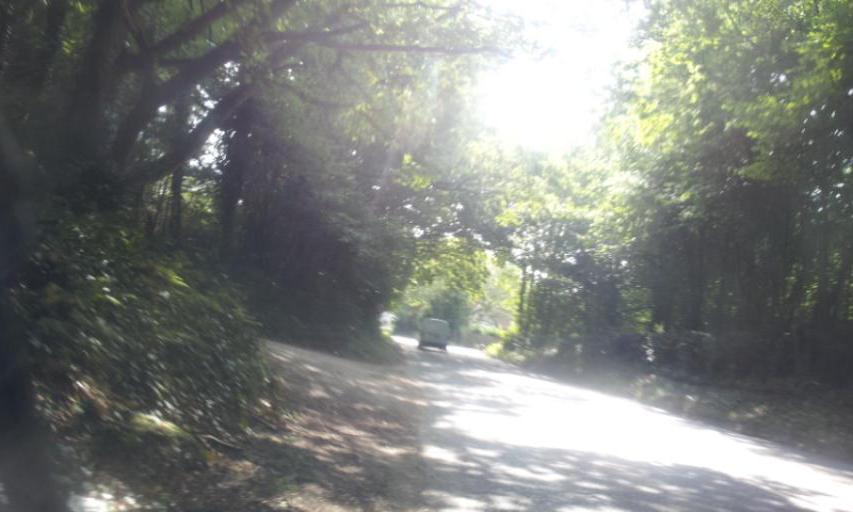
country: GB
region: England
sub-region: Kent
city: Paddock Wood
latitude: 51.1647
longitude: 0.3838
